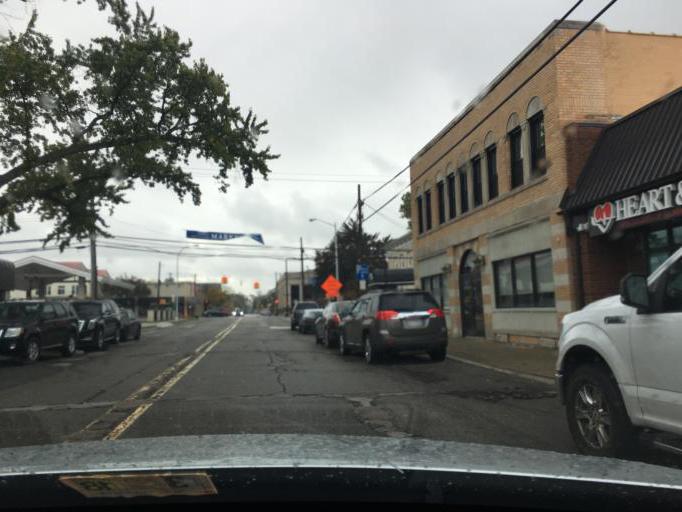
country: US
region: Michigan
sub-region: Wayne County
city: Dearborn Heights
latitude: 42.3067
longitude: -83.2464
